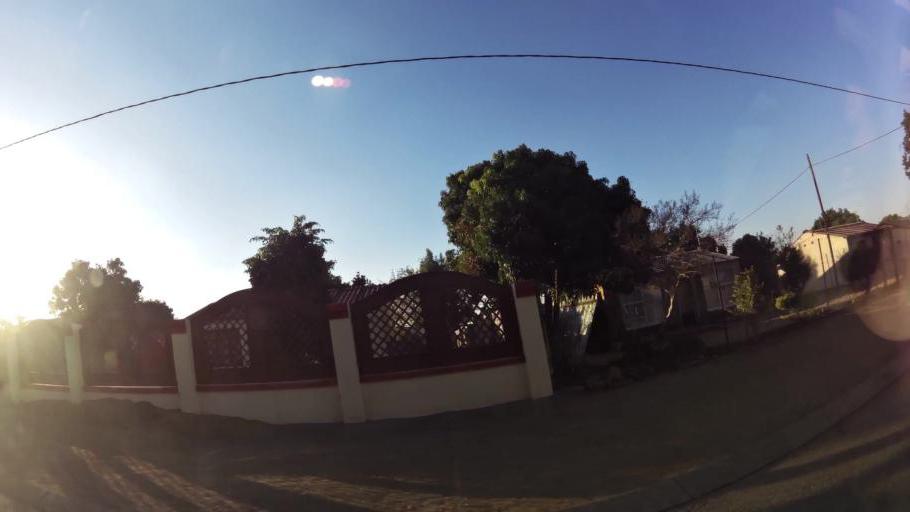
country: ZA
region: North-West
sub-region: Bojanala Platinum District Municipality
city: Rustenburg
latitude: -25.6314
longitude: 27.2130
